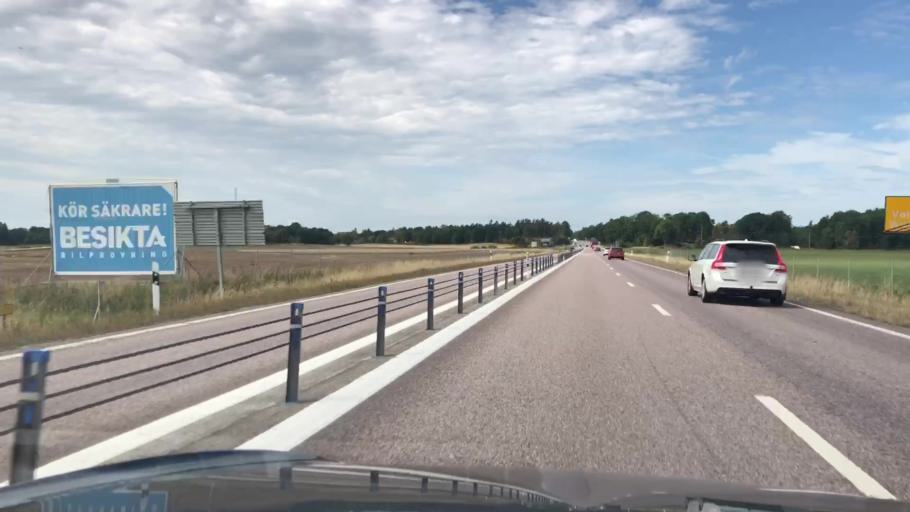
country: SE
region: Blekinge
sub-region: Ronneby Kommun
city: Kallinge
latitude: 56.2008
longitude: 15.3675
